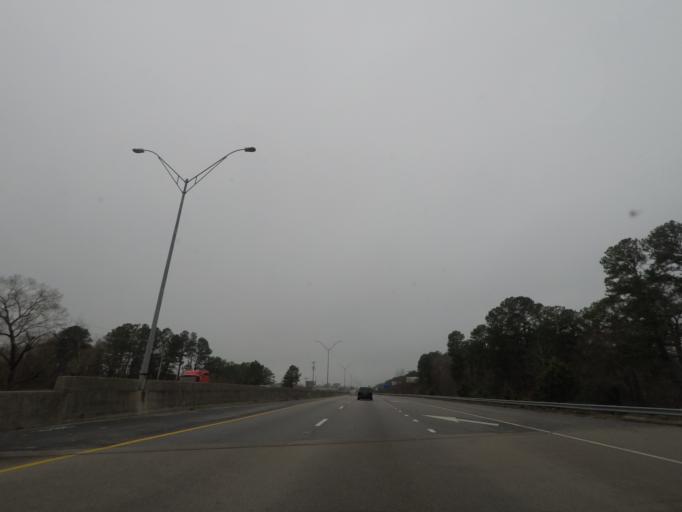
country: US
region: North Carolina
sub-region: Robeson County
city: Lumberton
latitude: 34.6321
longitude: -79.0303
